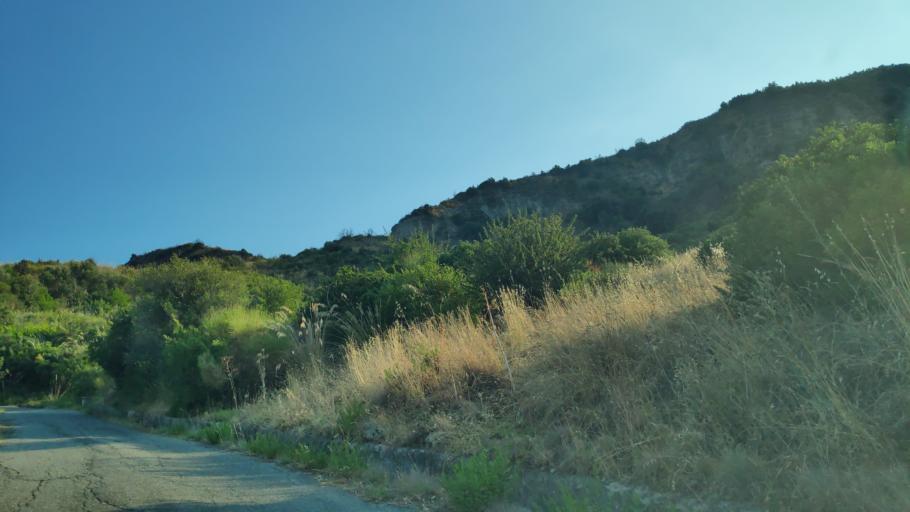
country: IT
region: Calabria
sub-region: Provincia di Reggio Calabria
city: Placanica
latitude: 38.4100
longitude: 16.4357
